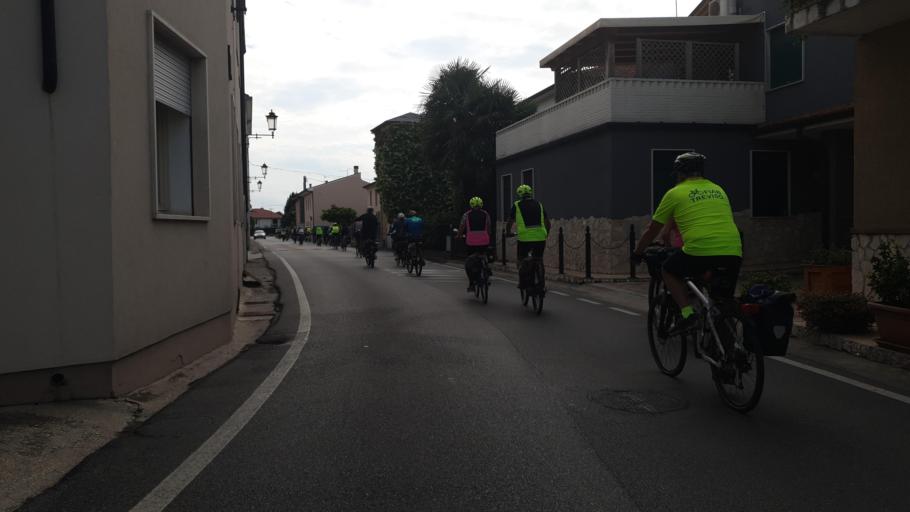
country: IT
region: Veneto
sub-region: Provincia di Vicenza
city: Noventa Vicentina
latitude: 45.2920
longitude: 11.5358
